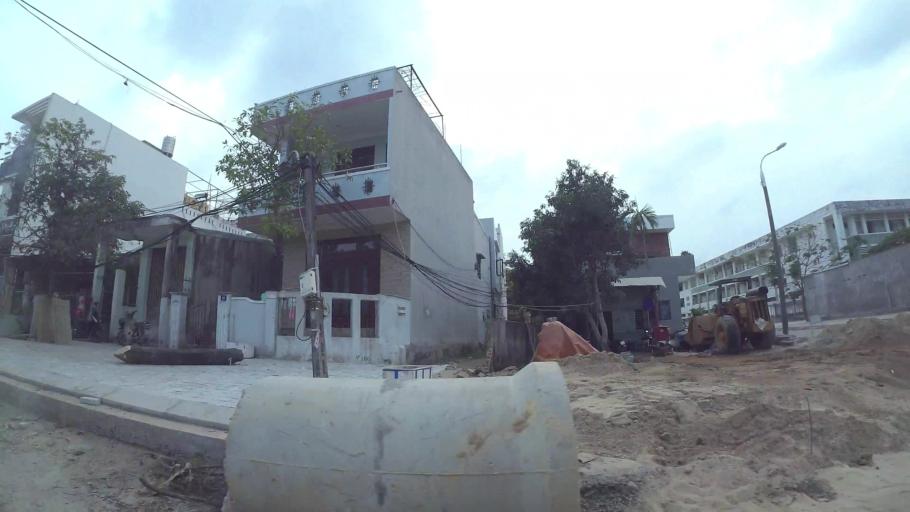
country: VN
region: Da Nang
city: Son Tra
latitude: 16.0592
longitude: 108.2446
